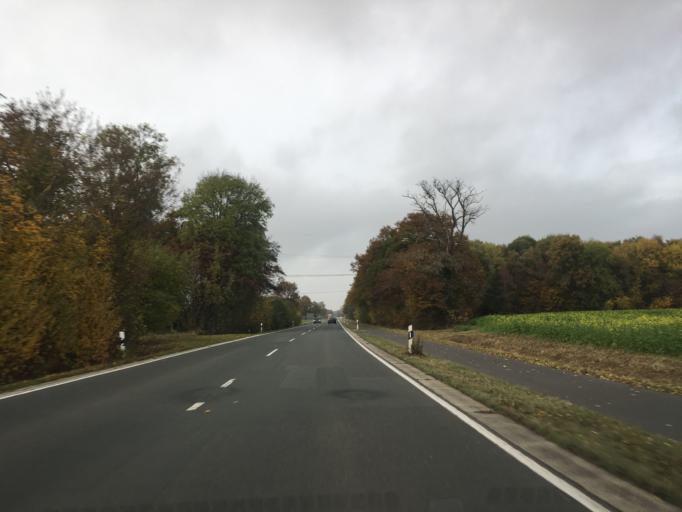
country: DE
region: North Rhine-Westphalia
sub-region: Regierungsbezirk Munster
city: Altenberge
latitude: 52.0770
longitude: 7.4322
